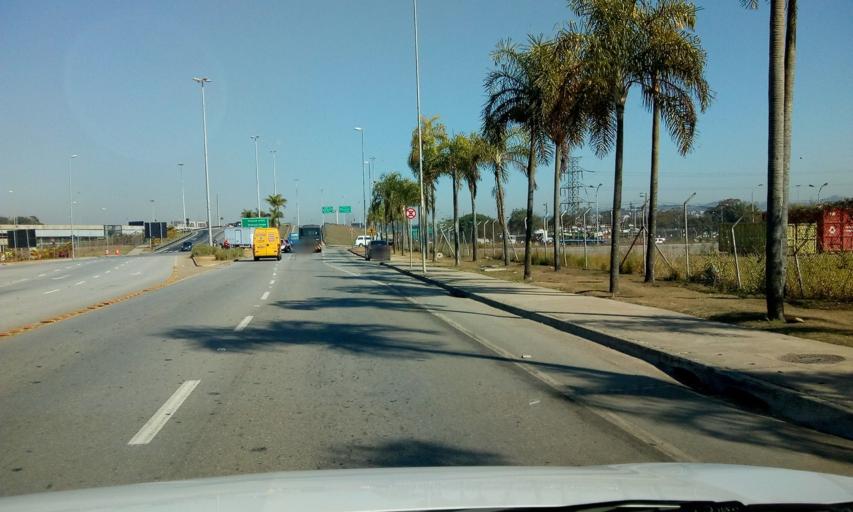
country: BR
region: Sao Paulo
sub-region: Guarulhos
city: Guarulhos
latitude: -23.4213
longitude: -46.4779
